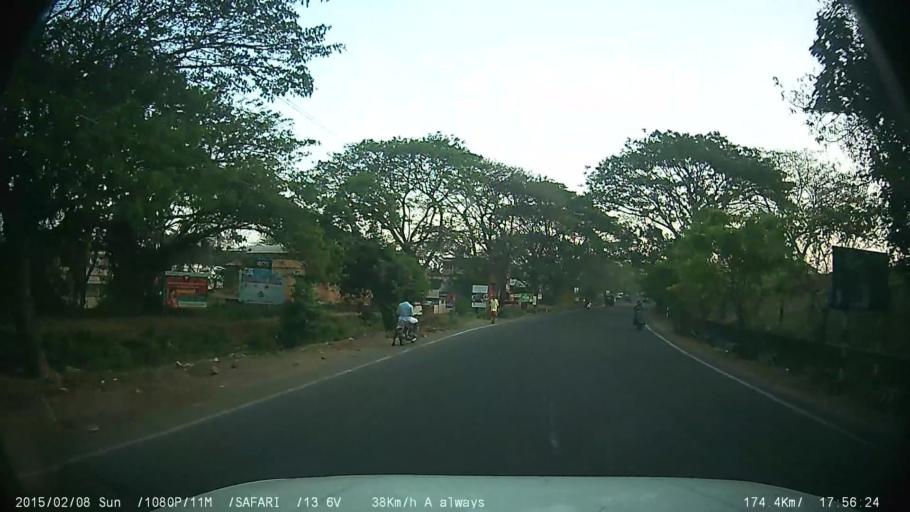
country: IN
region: Kerala
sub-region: Palakkad district
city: Palakkad
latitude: 10.7647
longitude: 76.6587
